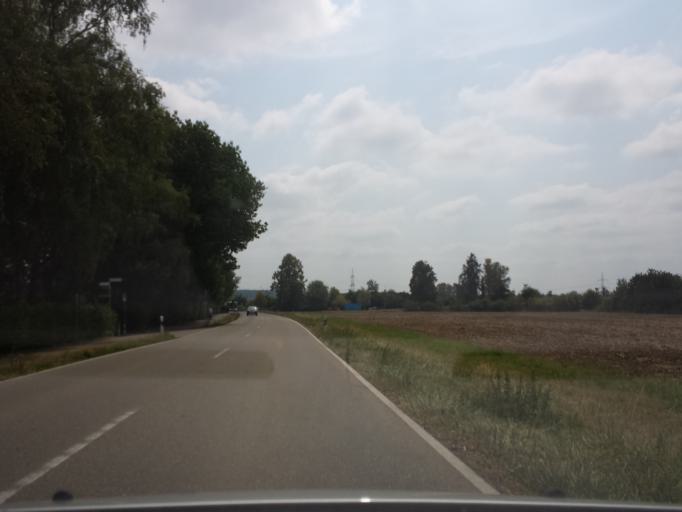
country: DE
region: Bavaria
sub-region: Swabia
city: Wasserburg
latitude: 48.4363
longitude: 10.2903
